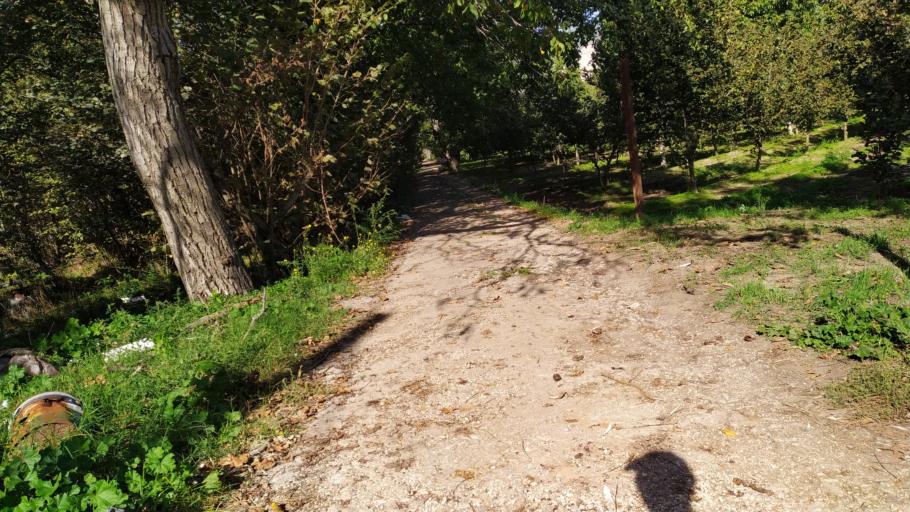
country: IT
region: Campania
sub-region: Provincia di Napoli
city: Camposano
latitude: 40.9636
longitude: 14.5176
